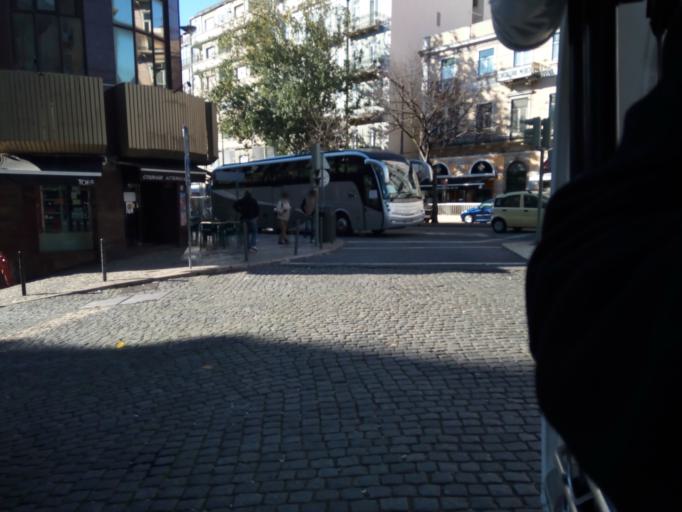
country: PT
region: Lisbon
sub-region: Lisbon
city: Lisbon
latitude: 38.7225
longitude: -9.1351
